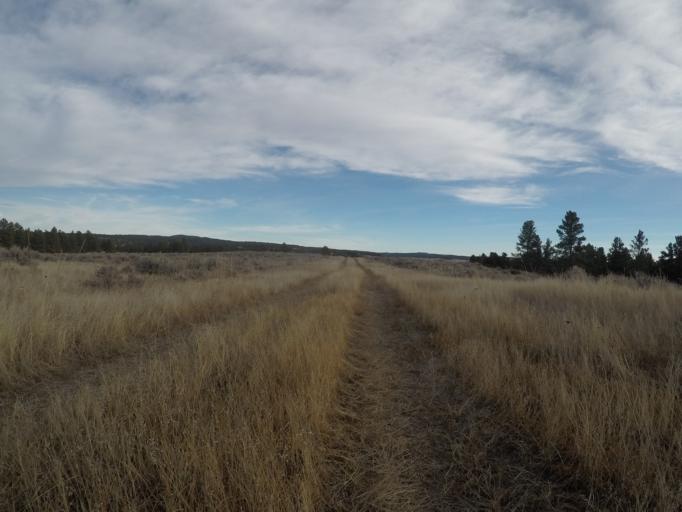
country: US
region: Montana
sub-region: Musselshell County
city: Roundup
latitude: 46.2737
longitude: -108.7472
